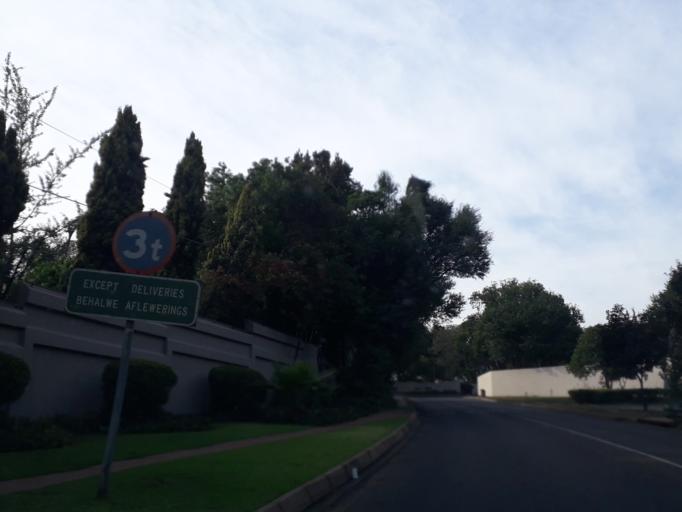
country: ZA
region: Gauteng
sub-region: City of Johannesburg Metropolitan Municipality
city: Johannesburg
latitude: -26.0897
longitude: 28.0372
